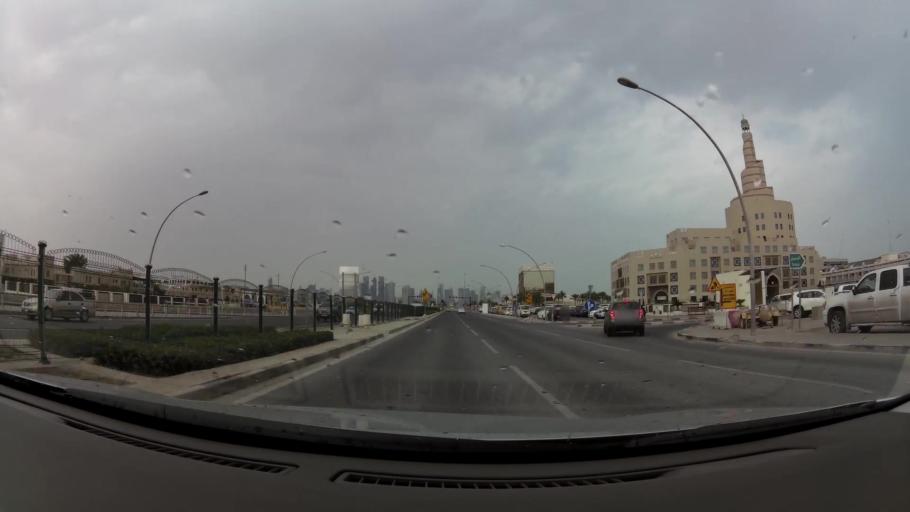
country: QA
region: Baladiyat ad Dawhah
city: Doha
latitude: 25.2874
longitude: 51.5347
